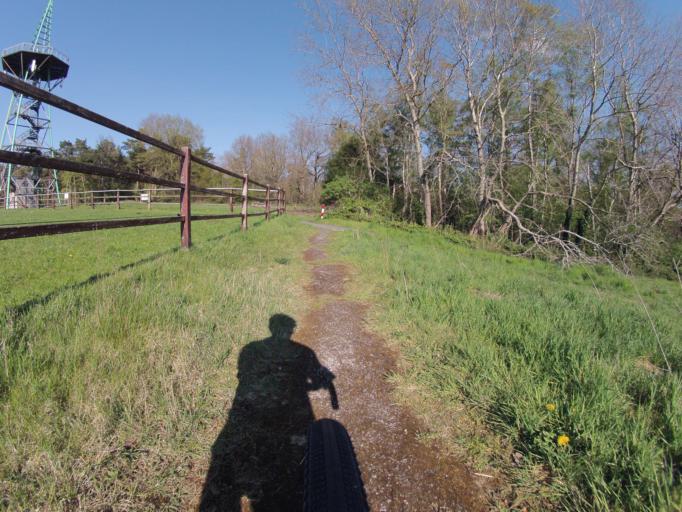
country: DE
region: Lower Saxony
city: Isterberg
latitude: 52.3530
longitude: 7.1483
